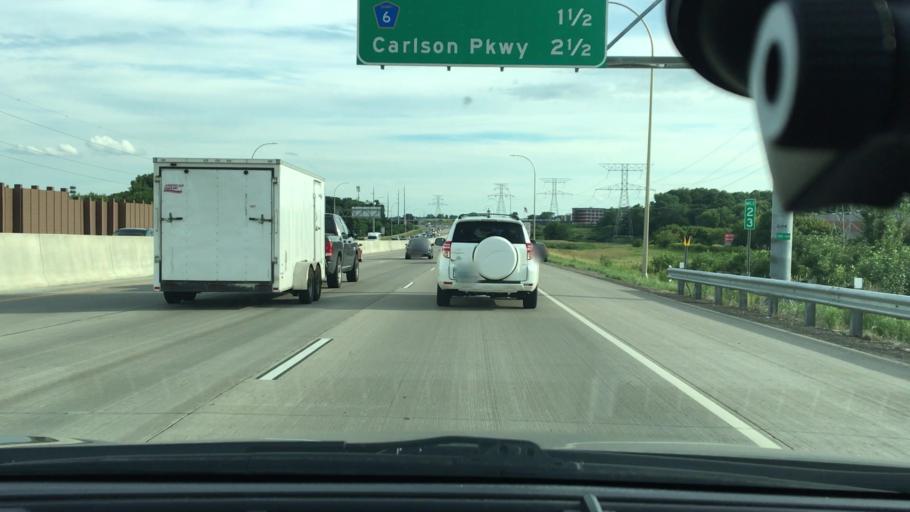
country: US
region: Minnesota
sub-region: Hennepin County
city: Plymouth
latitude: 45.0215
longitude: -93.4547
